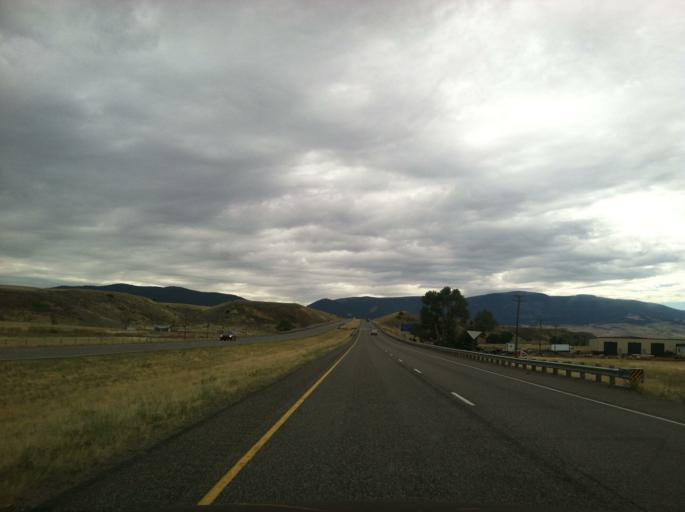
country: US
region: Montana
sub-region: Park County
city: Livingston
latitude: 45.6788
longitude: -110.5119
